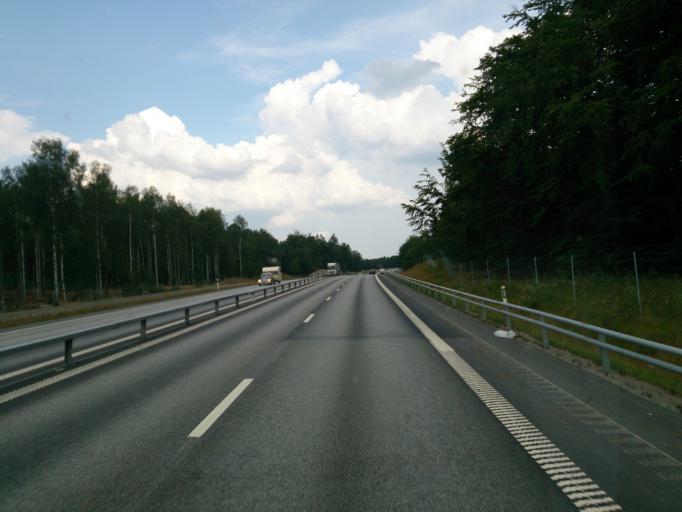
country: SE
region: Skane
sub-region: Horby Kommun
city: Hoerby
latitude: 55.9093
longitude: 13.7519
